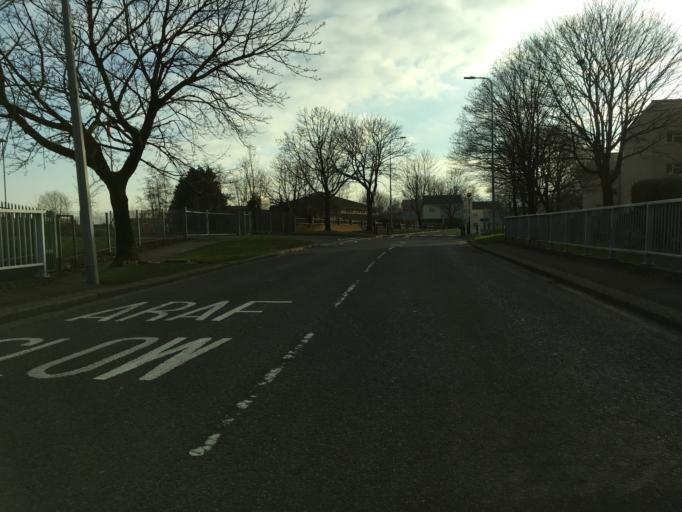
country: GB
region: Wales
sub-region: Cardiff
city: Cardiff
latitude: 51.5172
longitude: -3.1514
